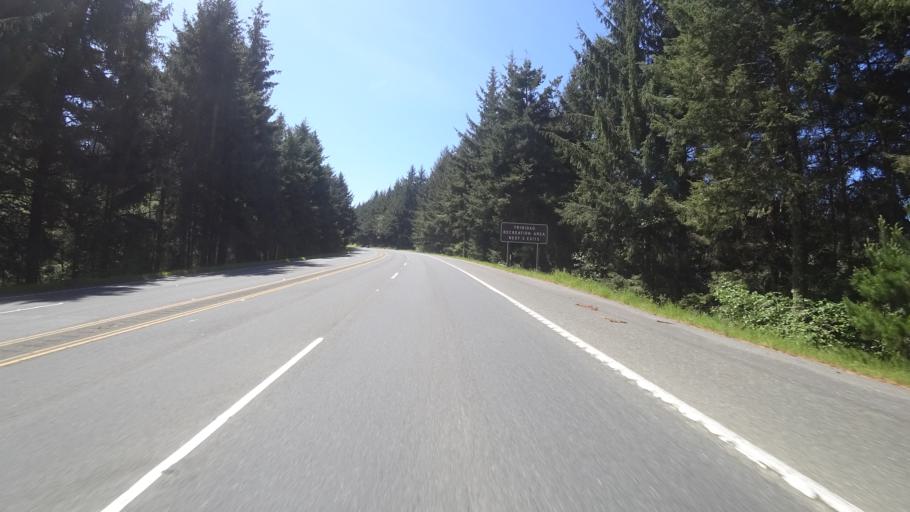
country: US
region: California
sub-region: Humboldt County
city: Westhaven-Moonstone
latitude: 41.1503
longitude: -124.1355
